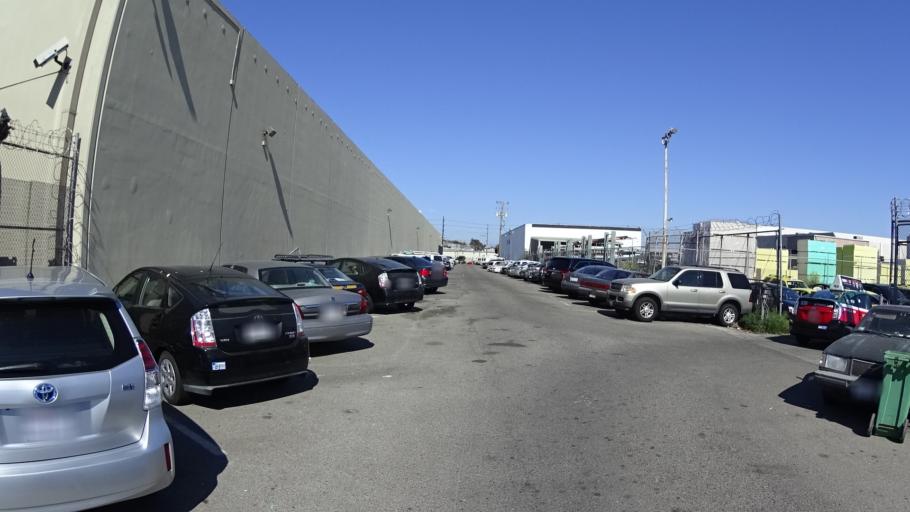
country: US
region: California
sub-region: San Francisco County
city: San Francisco
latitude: 37.7435
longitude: -122.4017
